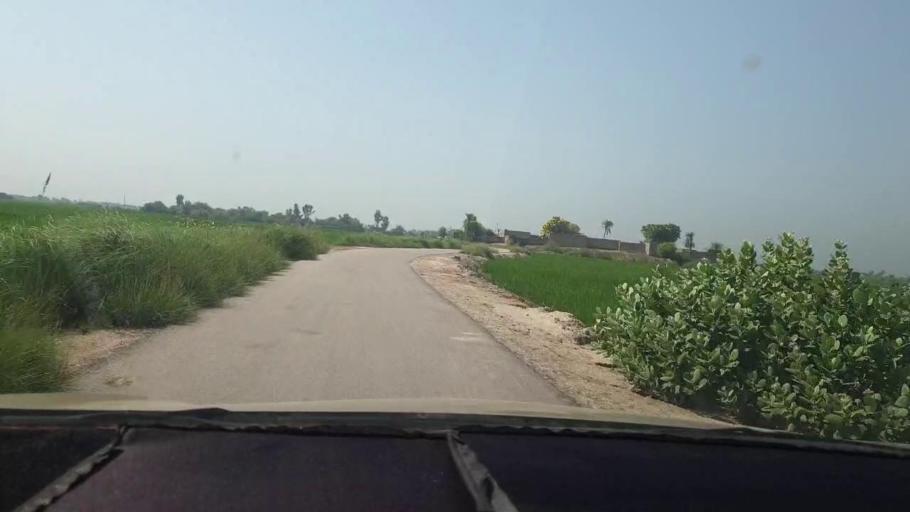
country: PK
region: Sindh
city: Kambar
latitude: 27.5627
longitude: 68.0442
